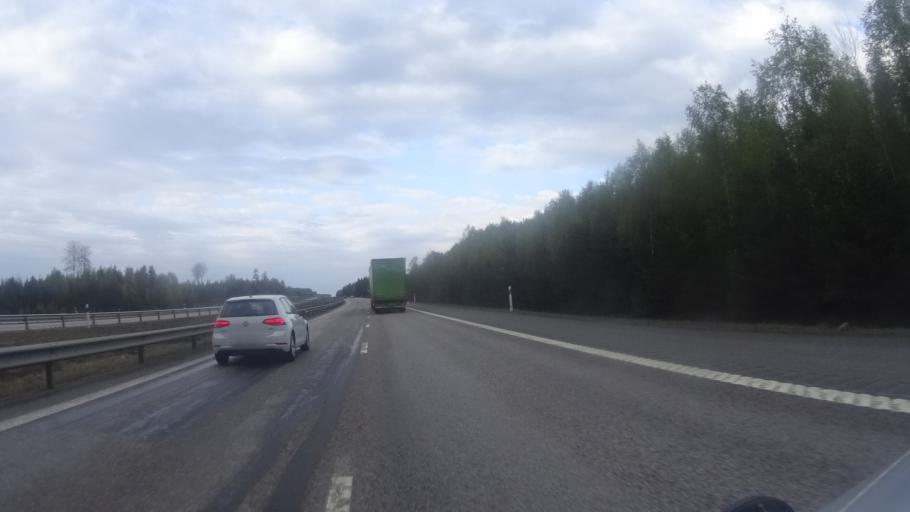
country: SE
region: Vaestmanland
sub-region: Arboga Kommun
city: Arboga
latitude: 59.3982
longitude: 15.7103
